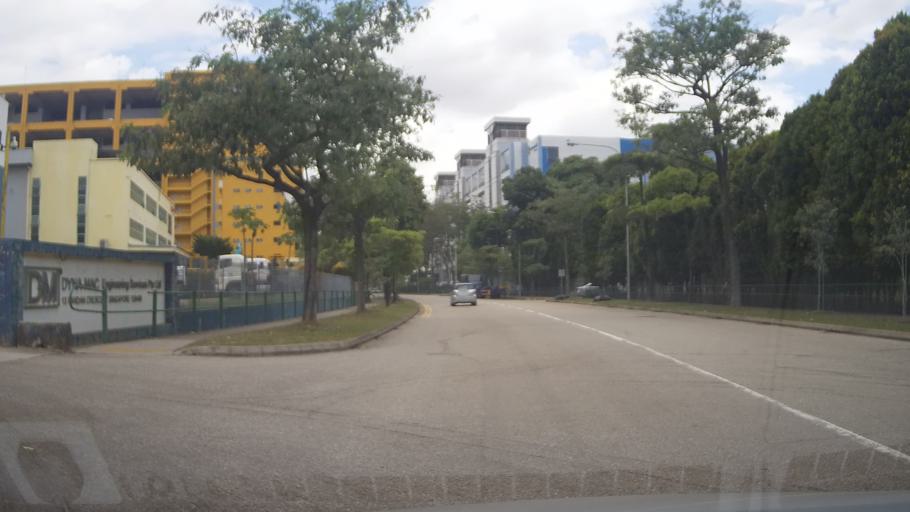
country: SG
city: Singapore
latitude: 1.3030
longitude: 103.7593
